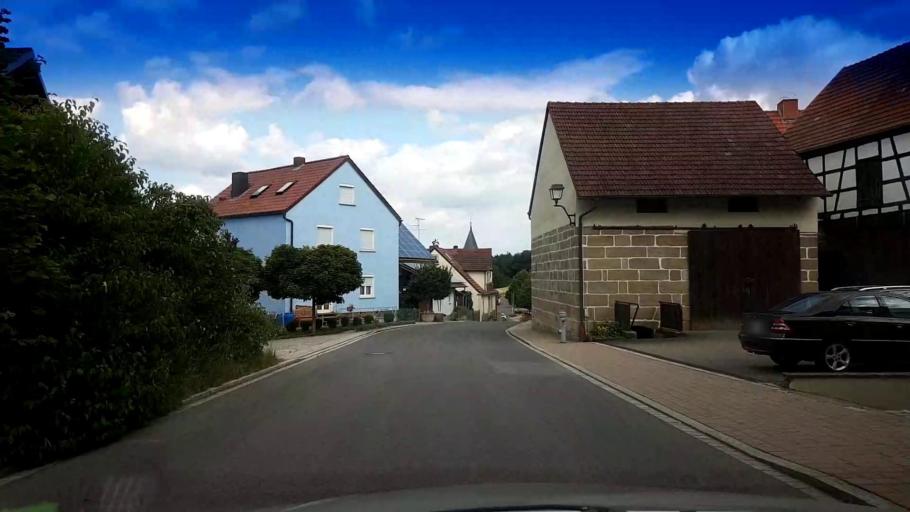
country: DE
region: Bavaria
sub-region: Upper Franconia
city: Gerach
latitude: 50.0033
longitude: 10.7909
